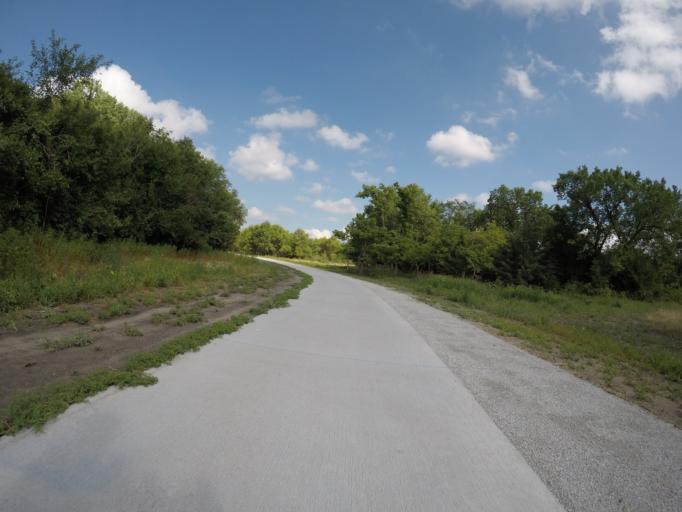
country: US
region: Nebraska
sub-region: Buffalo County
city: Kearney
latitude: 40.6764
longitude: -99.0056
